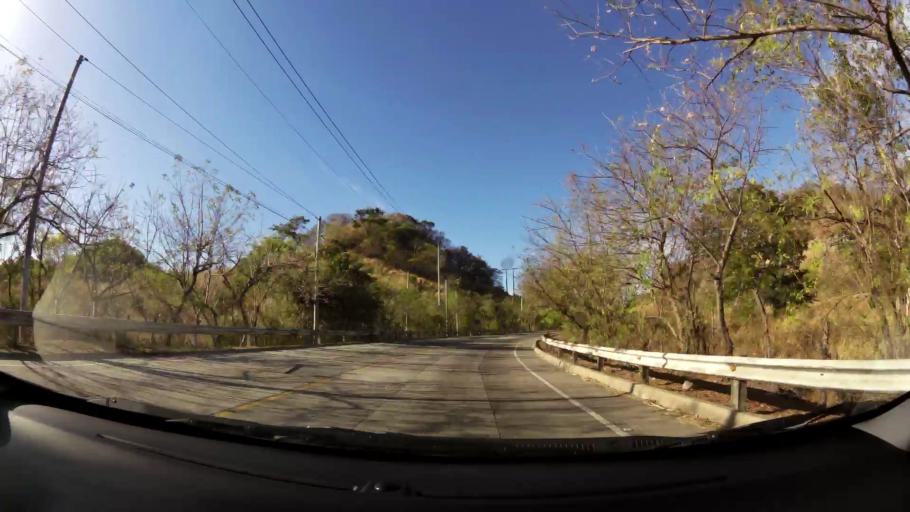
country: SV
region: Santa Ana
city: Texistepeque
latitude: 14.1439
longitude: -89.5142
